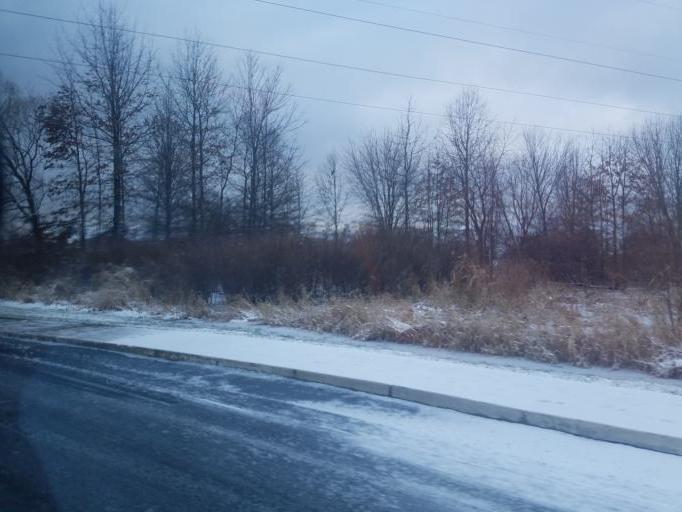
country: US
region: Ohio
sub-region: Franklin County
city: New Albany
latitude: 40.0570
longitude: -82.8461
